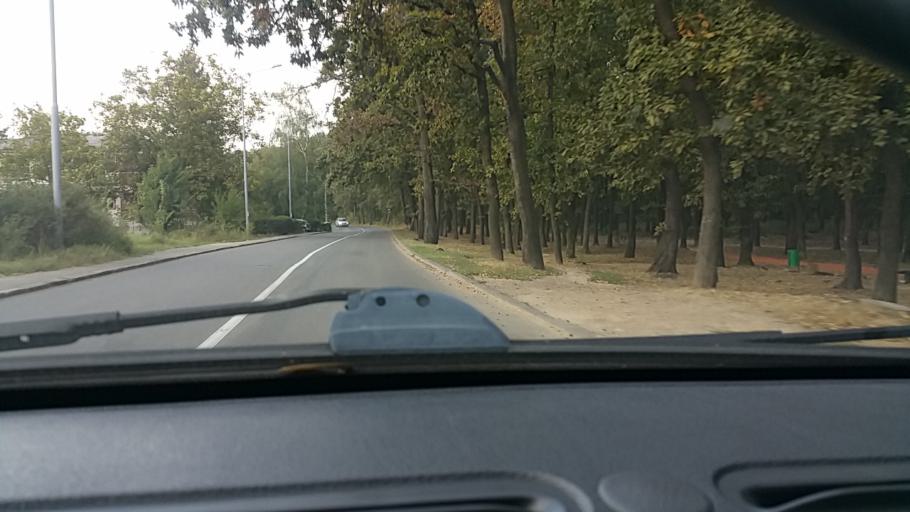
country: RS
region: Central Serbia
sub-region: Belgrade
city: Rakovica
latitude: 44.7445
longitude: 20.4621
